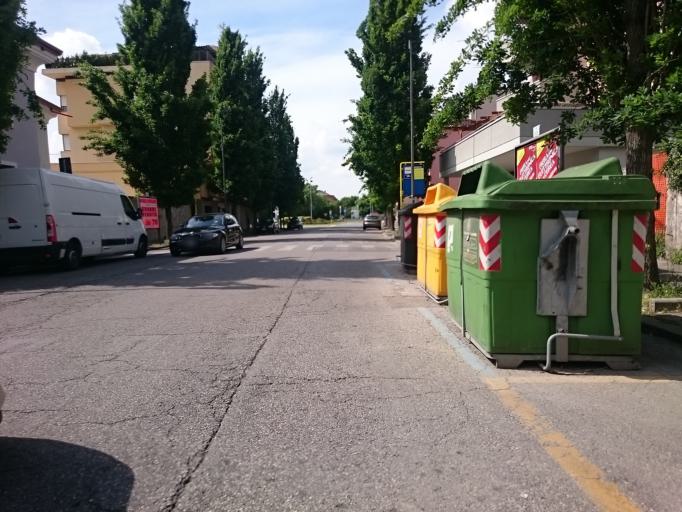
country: IT
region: Veneto
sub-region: Provincia di Rovigo
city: Rovigo
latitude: 45.0729
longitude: 11.7839
